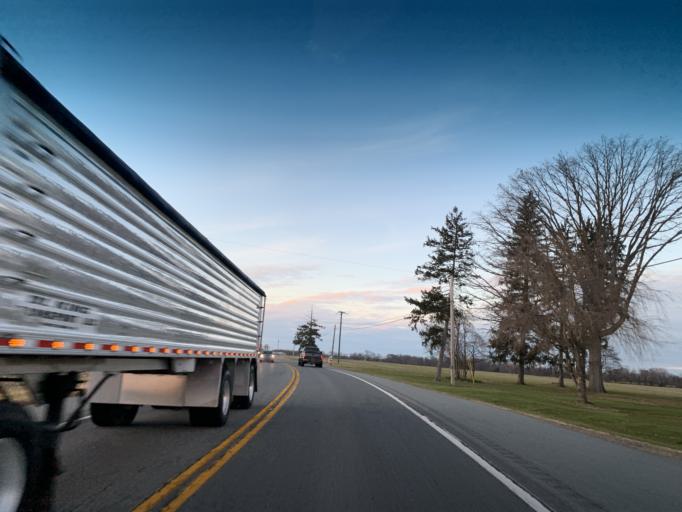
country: US
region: Delaware
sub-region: New Castle County
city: Middletown
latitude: 39.4390
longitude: -75.8623
